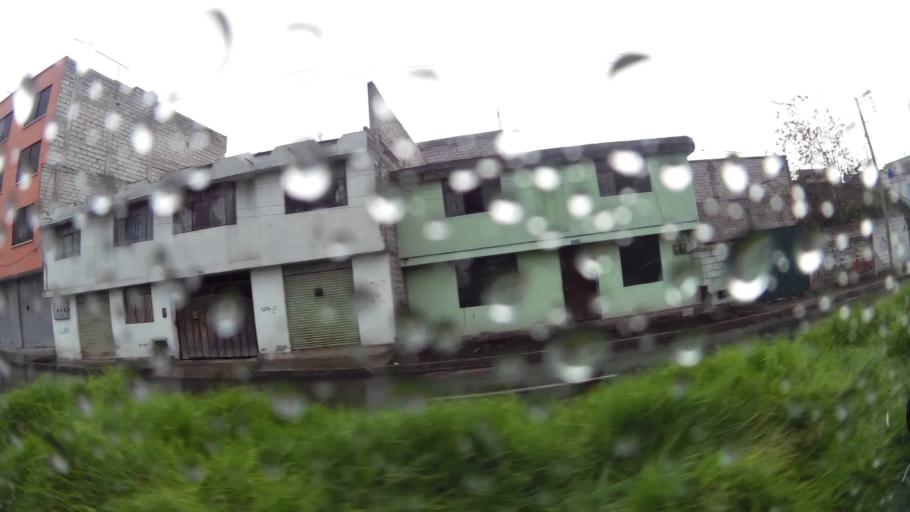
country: EC
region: Pichincha
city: Quito
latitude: -0.3102
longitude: -78.5477
